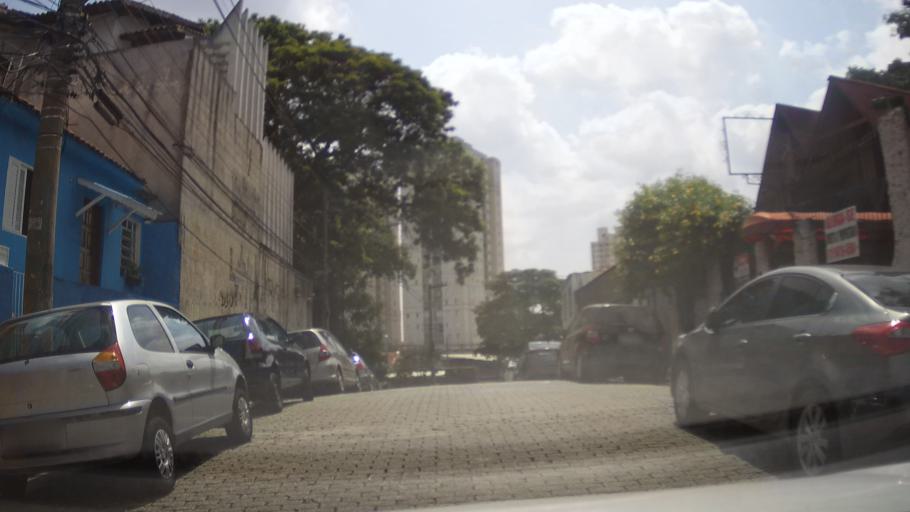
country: BR
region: Sao Paulo
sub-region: Guarulhos
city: Guarulhos
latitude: -23.4685
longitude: -46.5368
